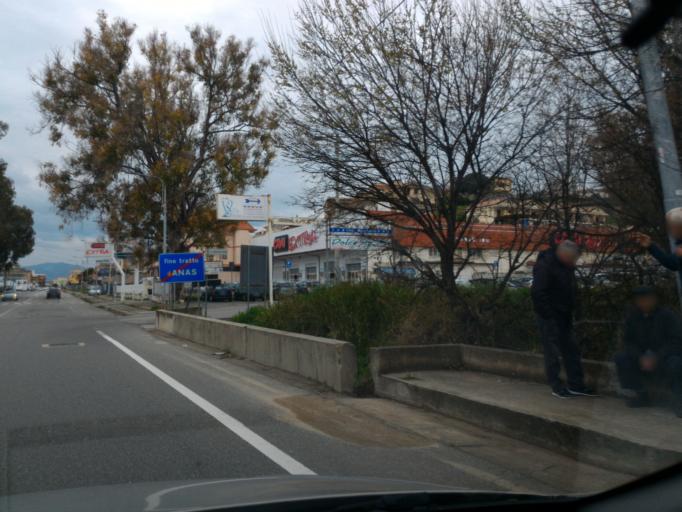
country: IT
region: Calabria
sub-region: Provincia di Catanzaro
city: Barone
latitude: 38.8343
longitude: 16.6344
